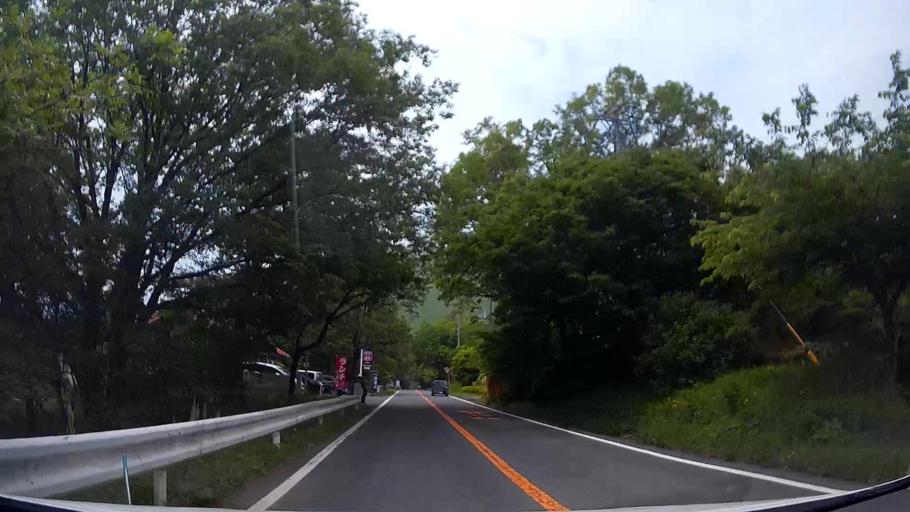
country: JP
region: Shizuoka
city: Ito
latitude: 34.9007
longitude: 139.1035
